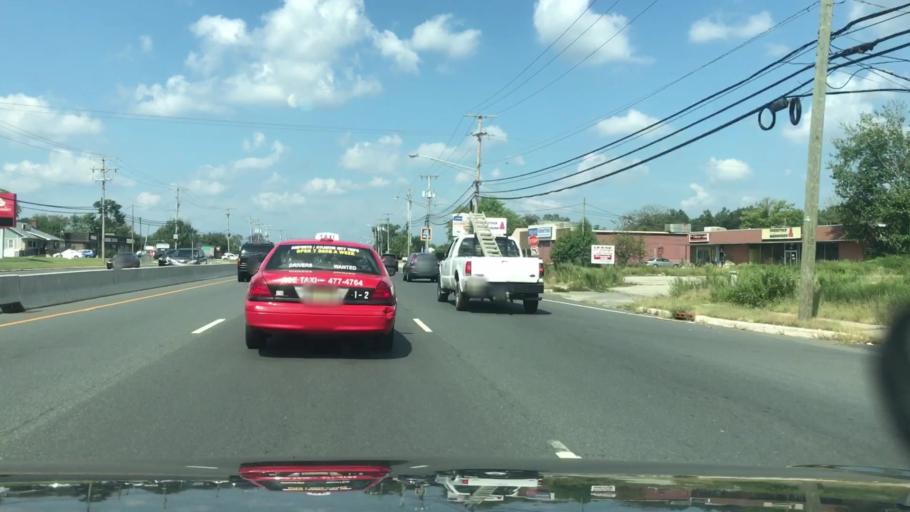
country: US
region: New Jersey
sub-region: Ocean County
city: Silver Ridge
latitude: 39.9691
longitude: -74.2320
